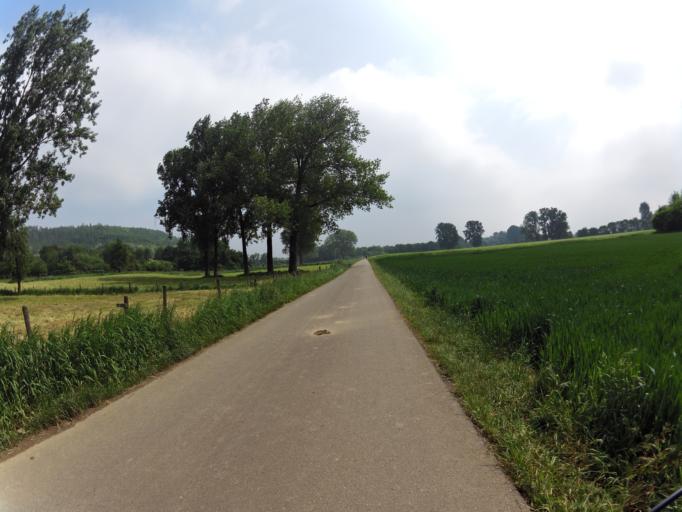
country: DE
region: North Rhine-Westphalia
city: Huckelhoven
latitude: 51.0536
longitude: 6.1997
